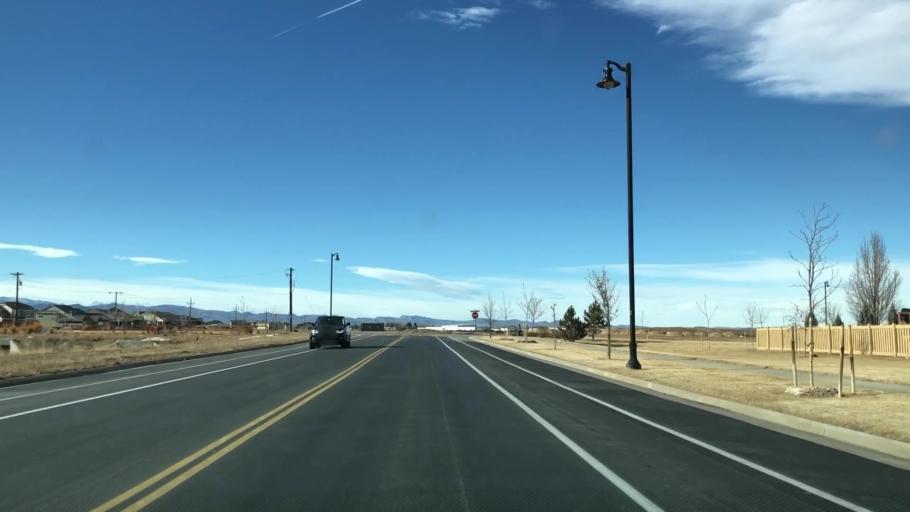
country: US
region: Colorado
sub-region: Weld County
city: Windsor
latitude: 40.5108
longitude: -104.9520
